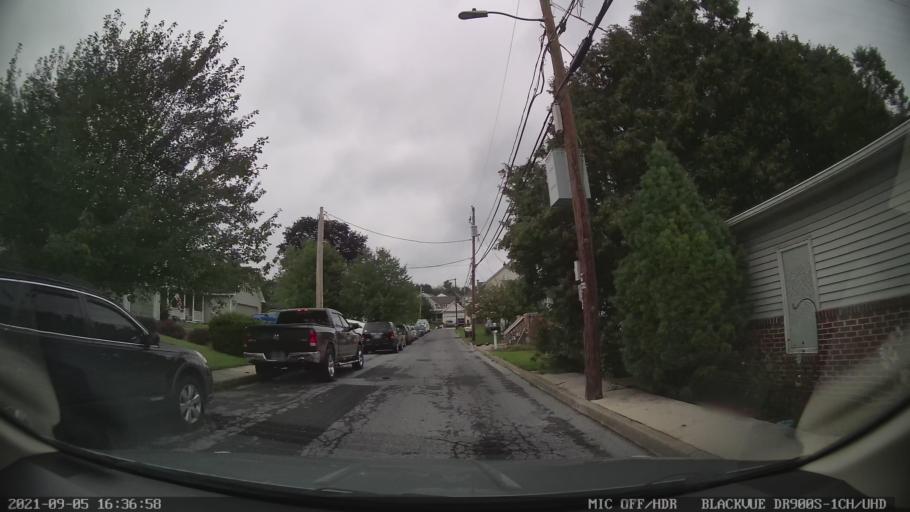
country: US
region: Pennsylvania
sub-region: Northampton County
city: Northampton
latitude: 40.6801
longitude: -75.5023
